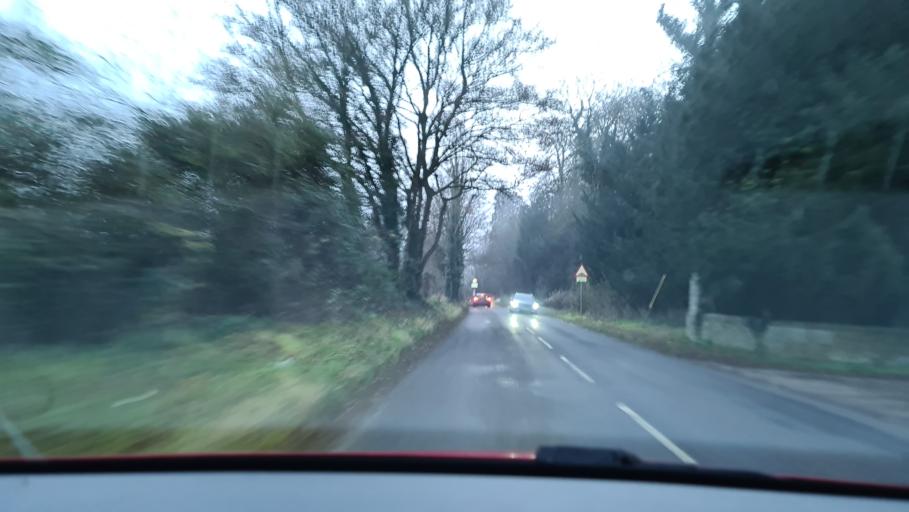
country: GB
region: England
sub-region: Oxfordshire
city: Bicester
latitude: 51.8949
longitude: -1.1875
